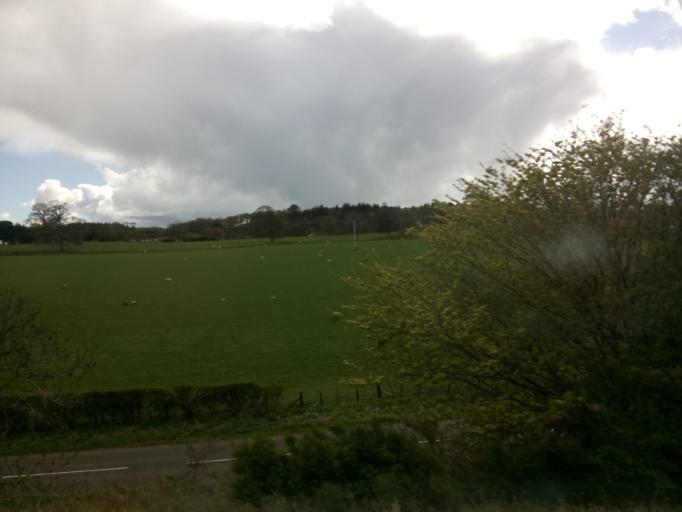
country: GB
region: Scotland
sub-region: East Lothian
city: Dunbar
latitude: 55.9440
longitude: -2.3755
